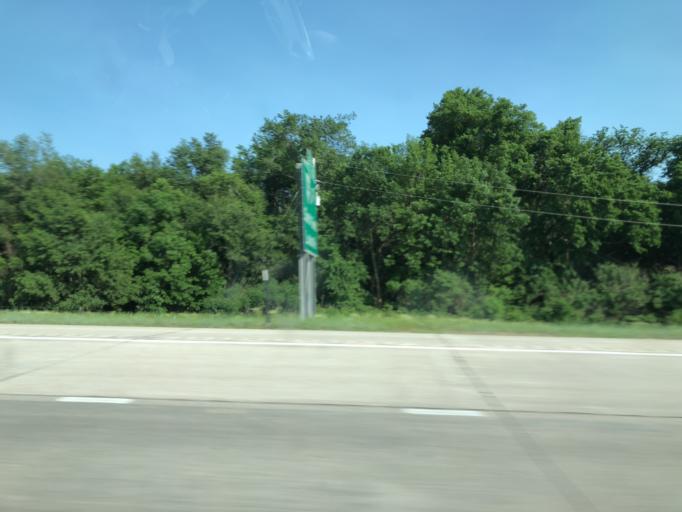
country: US
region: Nebraska
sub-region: Saunders County
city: Ashland
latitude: 41.0065
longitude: -96.3131
